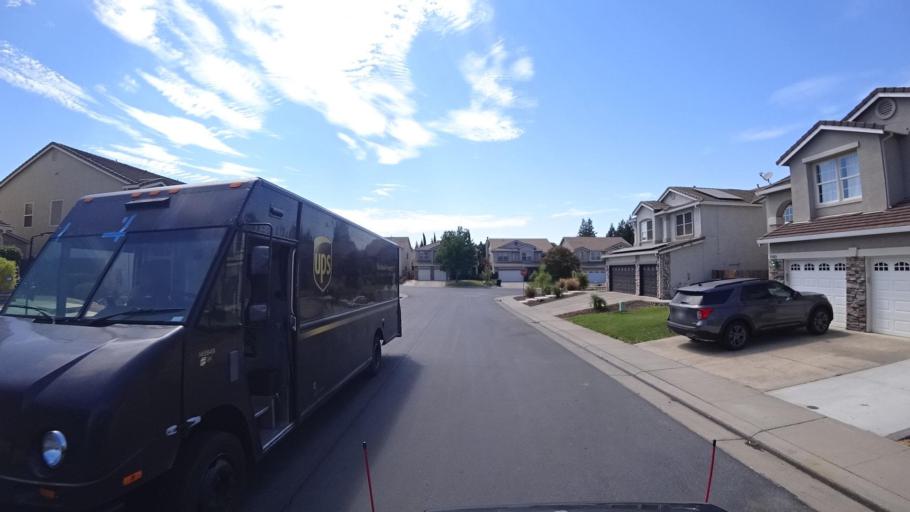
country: US
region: California
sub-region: Placer County
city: Roseville
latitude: 38.8015
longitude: -121.2902
